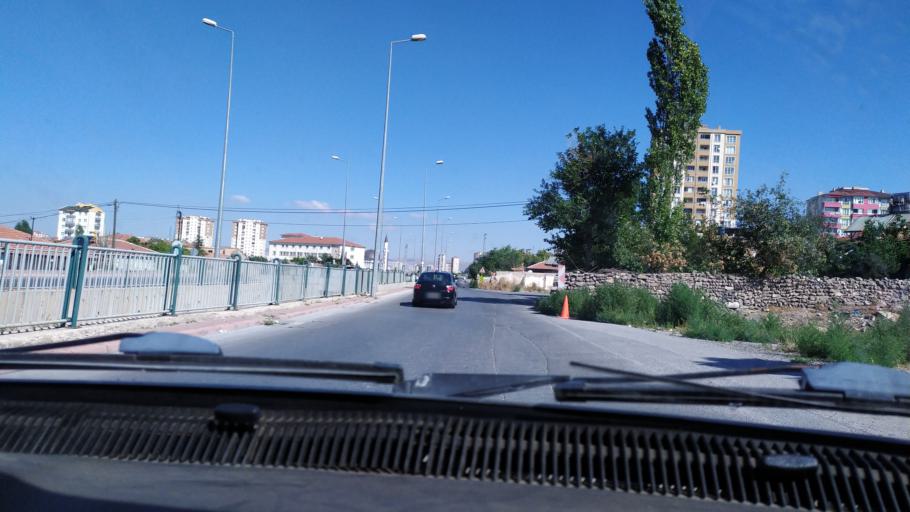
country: TR
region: Kayseri
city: Talas
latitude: 38.7274
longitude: 35.5506
